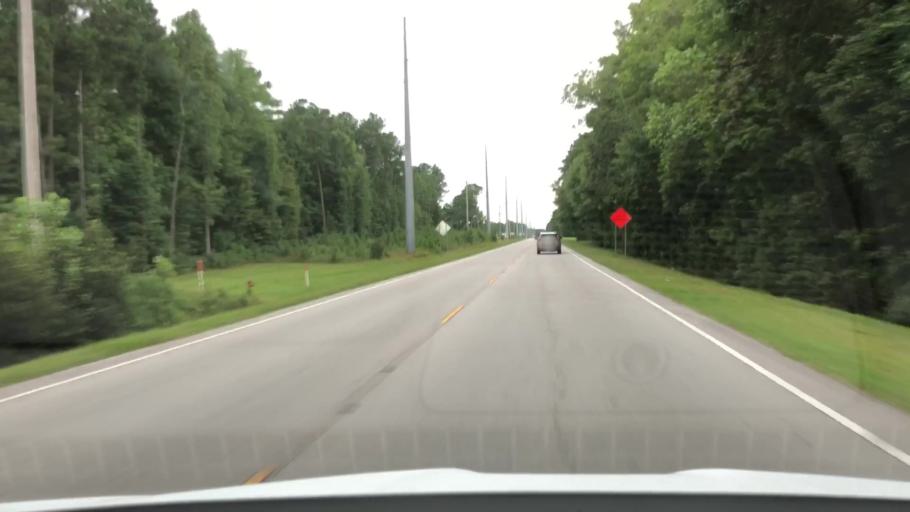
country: US
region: North Carolina
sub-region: Carteret County
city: Cape Carteret
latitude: 34.7336
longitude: -77.0808
